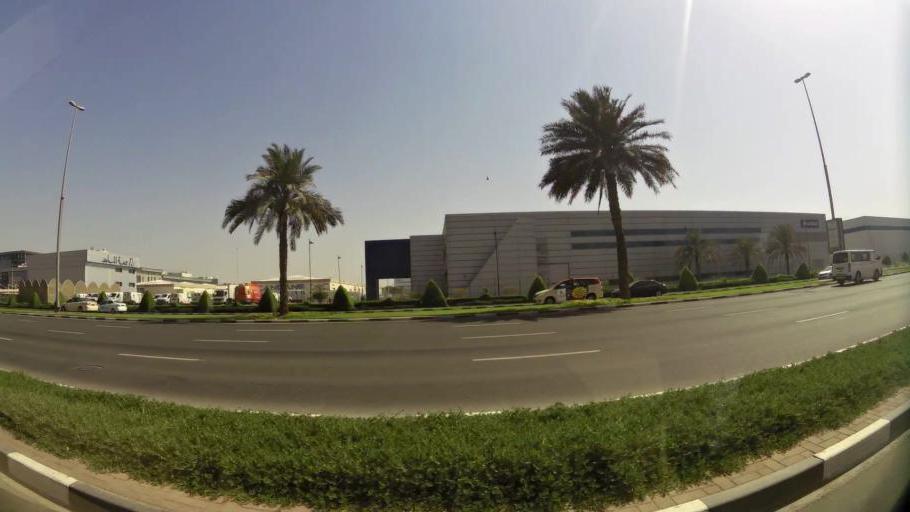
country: AE
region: Ash Shariqah
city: Sharjah
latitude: 25.2649
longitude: 55.3695
